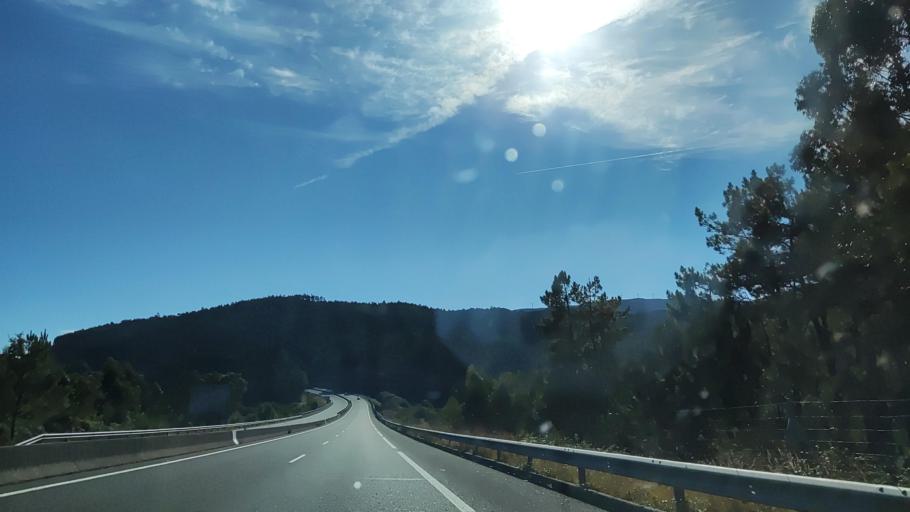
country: ES
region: Galicia
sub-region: Provincia da Coruna
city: Boiro
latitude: 42.6585
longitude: -8.8933
